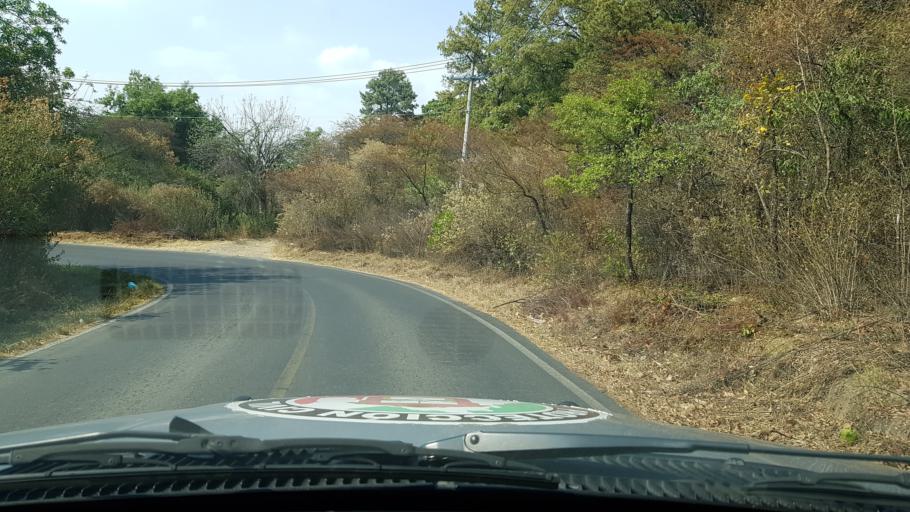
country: MX
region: Mexico
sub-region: Ozumba
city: San Jose Tlacotitlan
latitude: 18.9893
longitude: -98.8192
